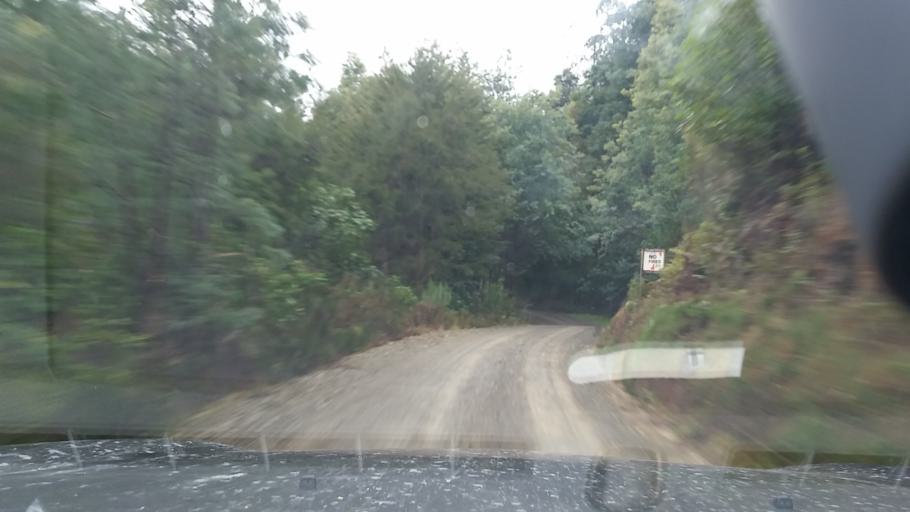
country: NZ
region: Nelson
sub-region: Nelson City
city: Nelson
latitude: -41.3749
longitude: 173.5964
